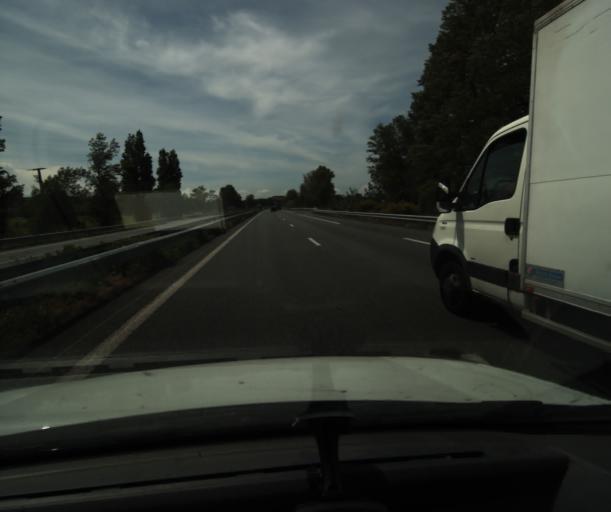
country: FR
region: Languedoc-Roussillon
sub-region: Departement de l'Aude
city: Castelnaudary
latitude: 43.2855
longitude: 1.9613
